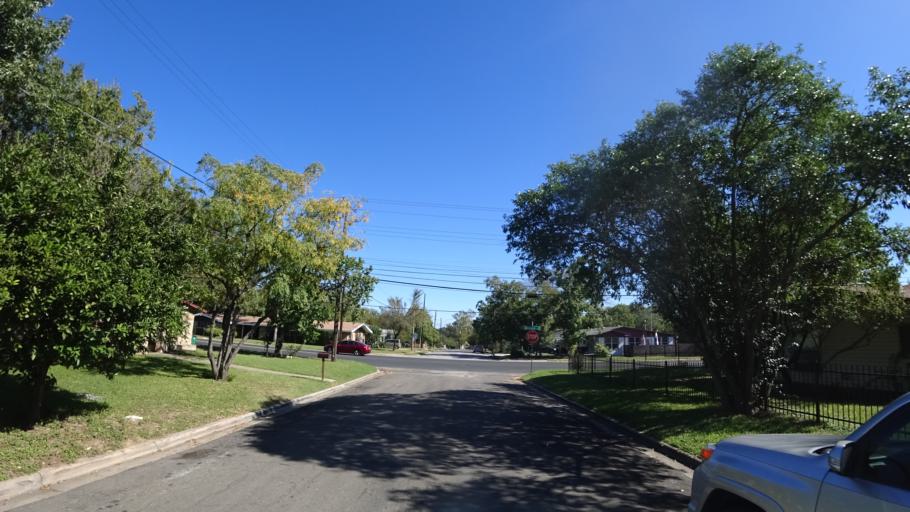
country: US
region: Texas
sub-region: Travis County
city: Austin
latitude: 30.2834
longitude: -97.6847
